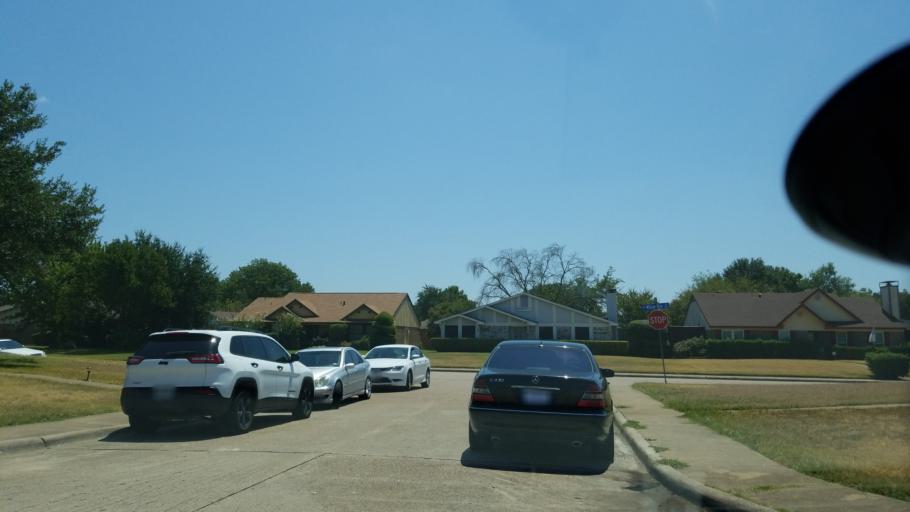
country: US
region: Texas
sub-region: Dallas County
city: Duncanville
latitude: 32.6358
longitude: -96.8860
